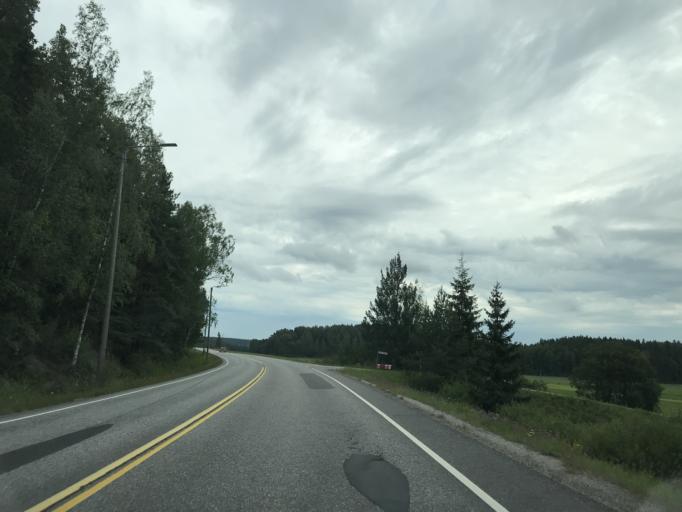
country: FI
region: Varsinais-Suomi
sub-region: Turku
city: Paimio
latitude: 60.4293
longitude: 22.6150
